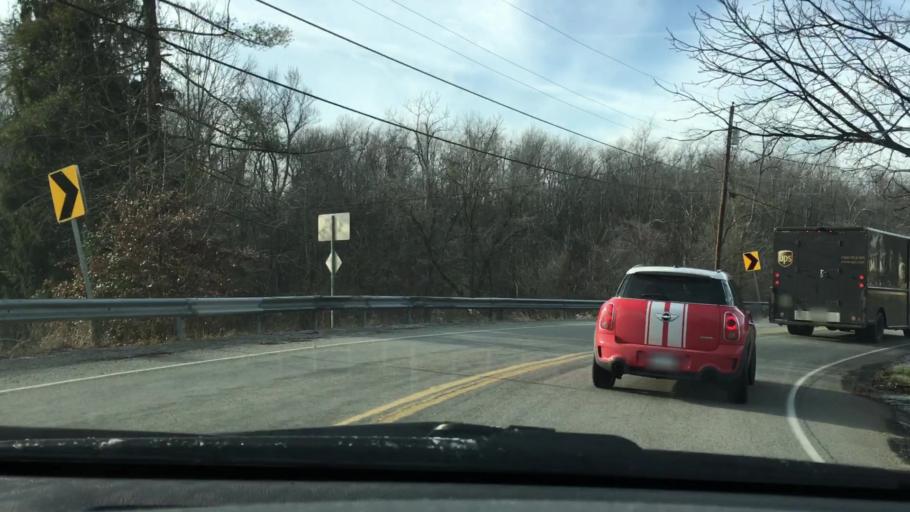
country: US
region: Pennsylvania
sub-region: Allegheny County
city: Industry
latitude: 40.2399
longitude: -79.7939
